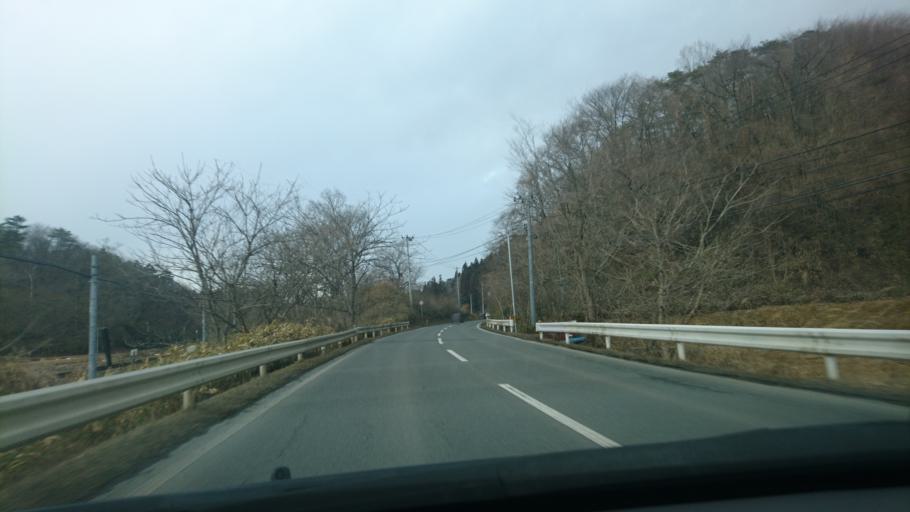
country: JP
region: Iwate
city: Ichinoseki
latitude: 38.9465
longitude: 141.3373
